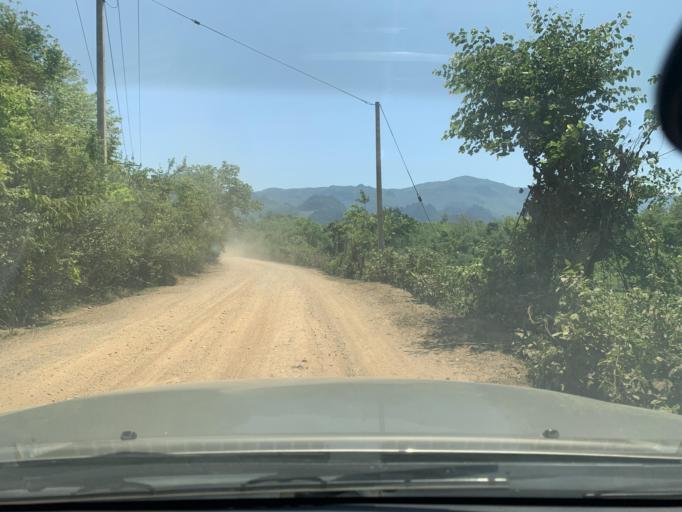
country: LA
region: Louangphabang
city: Louangphabang
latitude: 19.9062
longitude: 102.2376
